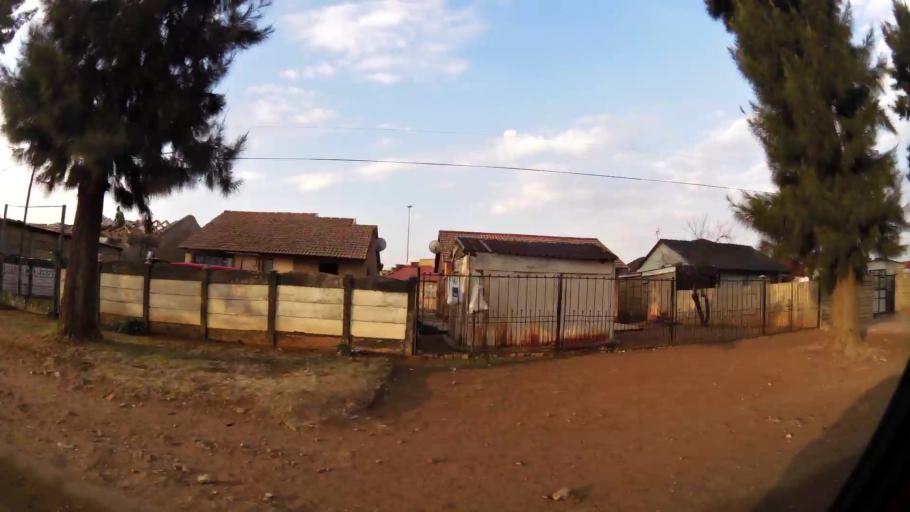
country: ZA
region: Gauteng
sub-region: City of Johannesburg Metropolitan Municipality
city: Orange Farm
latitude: -26.5915
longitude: 27.8230
